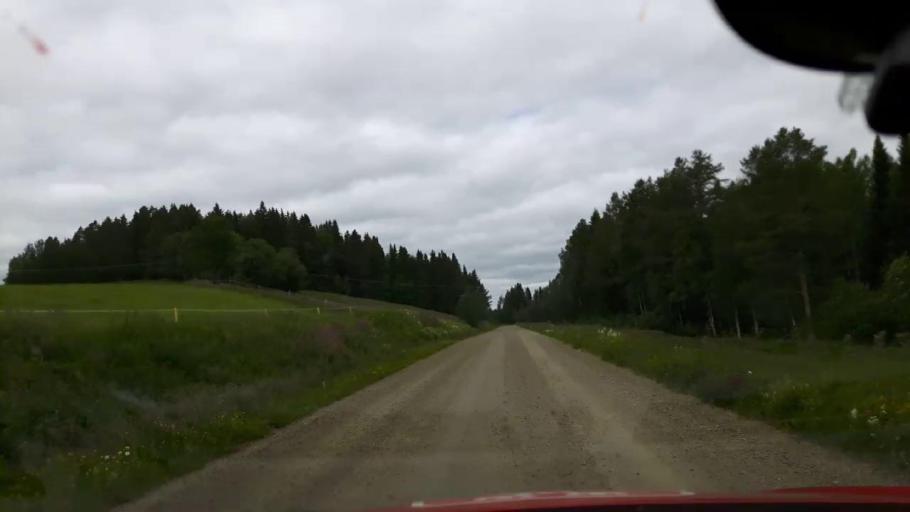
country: SE
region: Jaemtland
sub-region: OEstersunds Kommun
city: Brunflo
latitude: 62.9217
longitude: 15.0124
